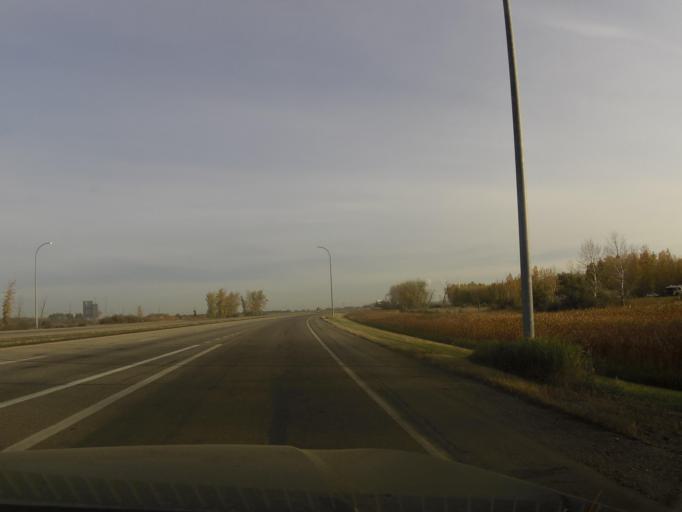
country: US
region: North Dakota
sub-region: Walsh County
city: Grafton
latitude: 48.5744
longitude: -97.1862
